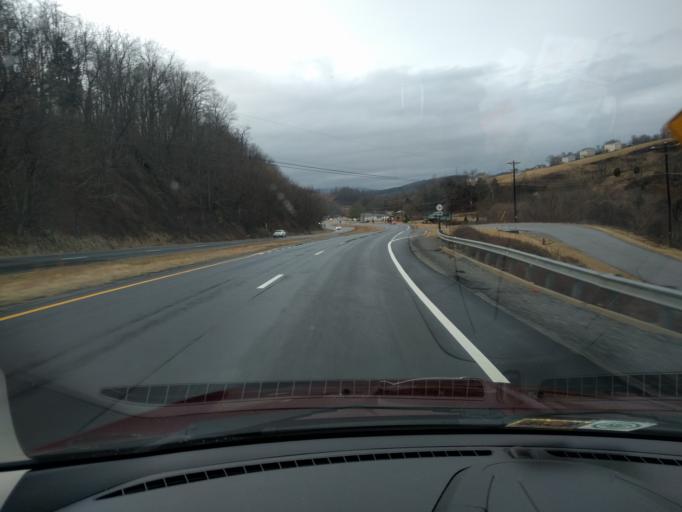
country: US
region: Virginia
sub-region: Giles County
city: Pembroke
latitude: 37.3194
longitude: -80.6115
